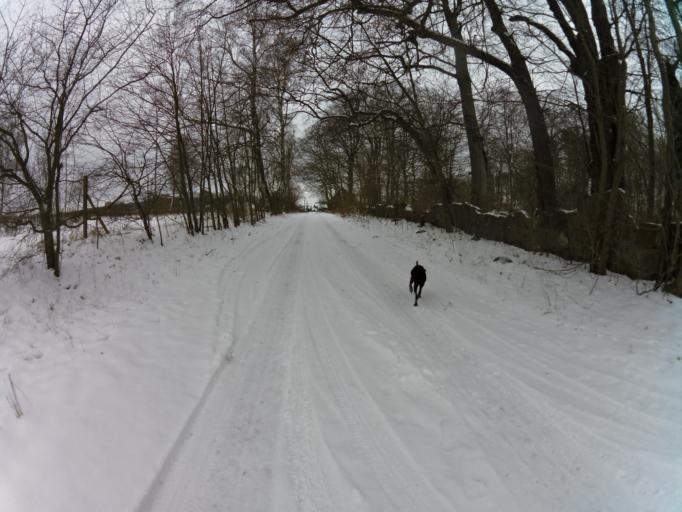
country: PL
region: West Pomeranian Voivodeship
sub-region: Powiat choszczenski
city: Recz
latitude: 53.3417
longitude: 15.5413
